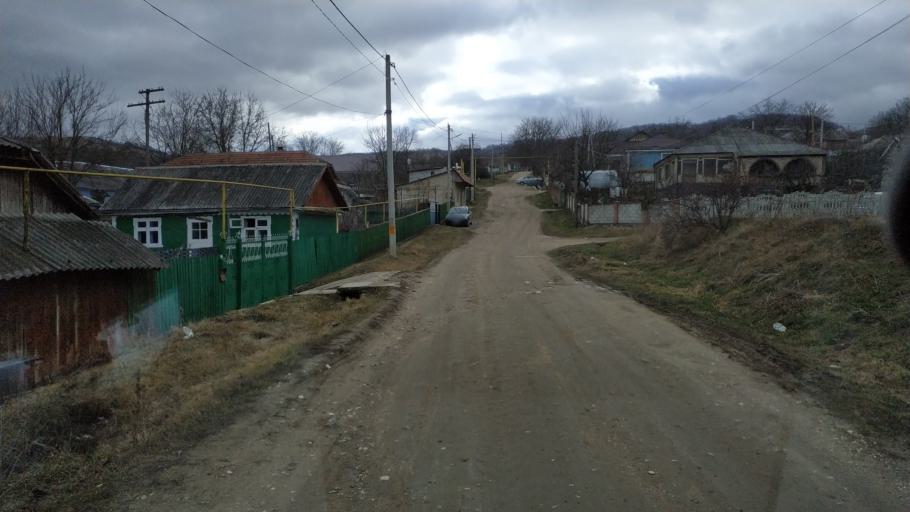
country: MD
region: Calarasi
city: Calarasi
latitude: 47.2376
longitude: 28.3104
